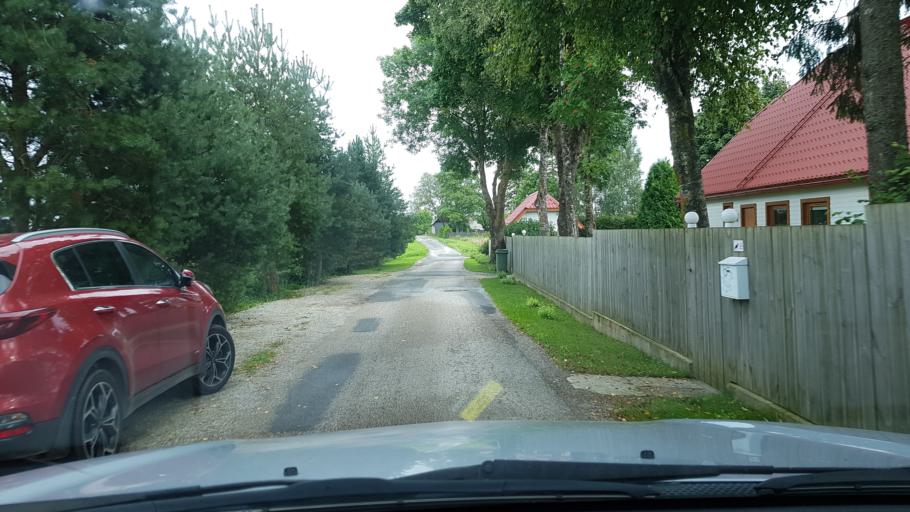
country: EE
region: Harju
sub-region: Joelaehtme vald
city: Loo
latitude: 59.4074
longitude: 24.9569
